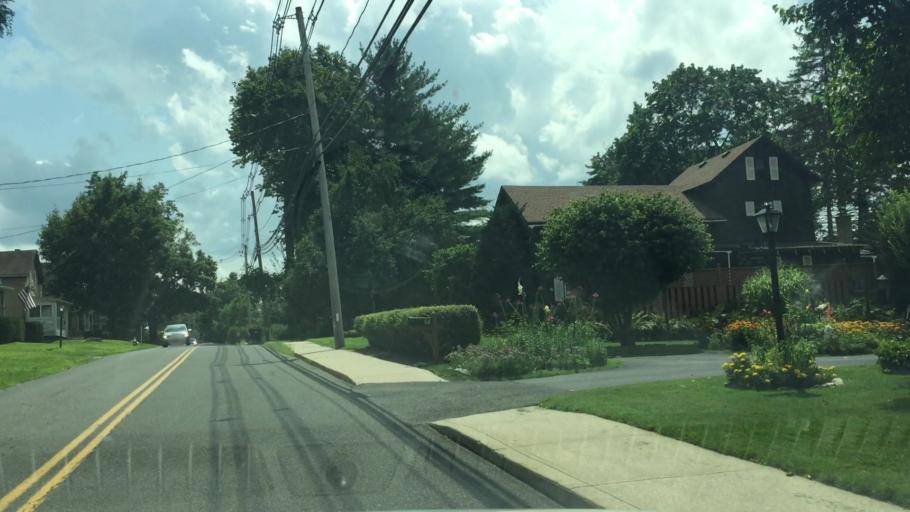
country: US
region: Massachusetts
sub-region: Berkshire County
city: Great Barrington
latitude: 42.1992
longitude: -73.3569
